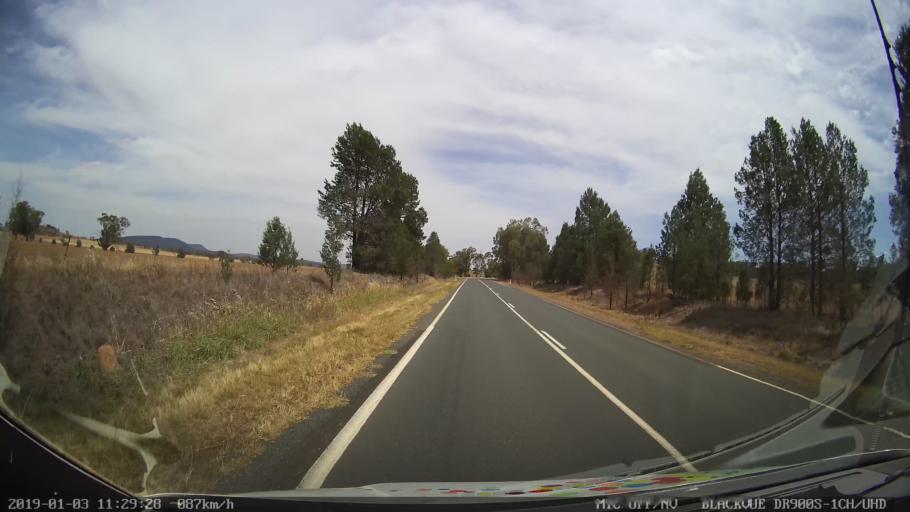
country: AU
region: New South Wales
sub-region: Weddin
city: Grenfell
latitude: -33.9921
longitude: 148.1981
